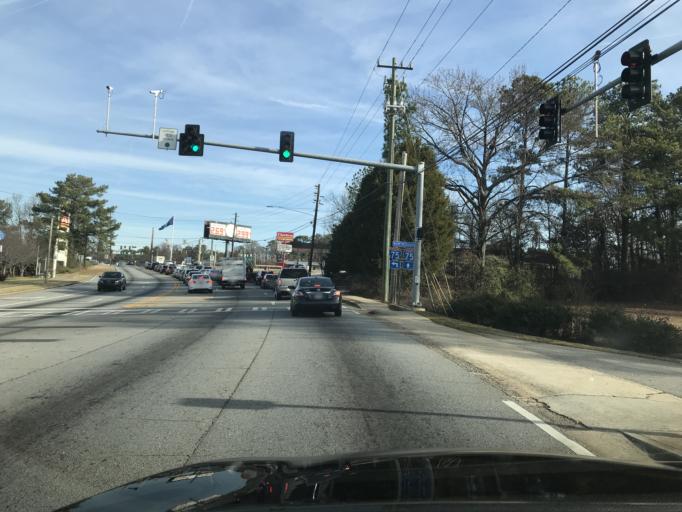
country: US
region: Georgia
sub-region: Clayton County
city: Riverdale
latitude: 33.5812
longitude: -84.3789
